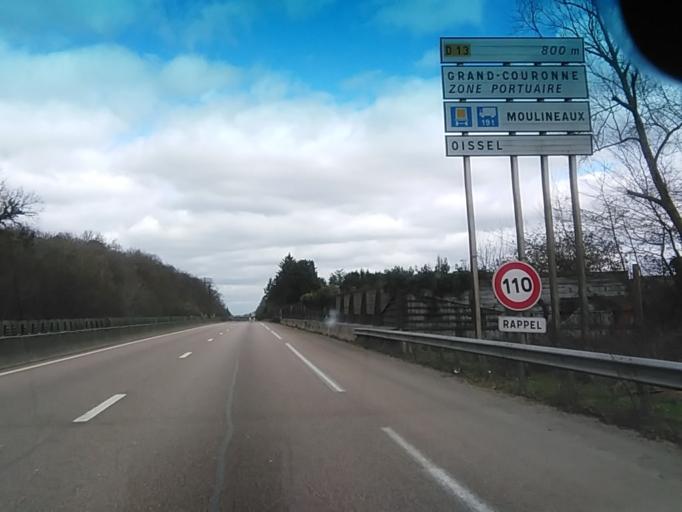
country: FR
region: Haute-Normandie
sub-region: Departement de la Seine-Maritime
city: Grand-Couronne
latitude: 49.3476
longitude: 1.0187
